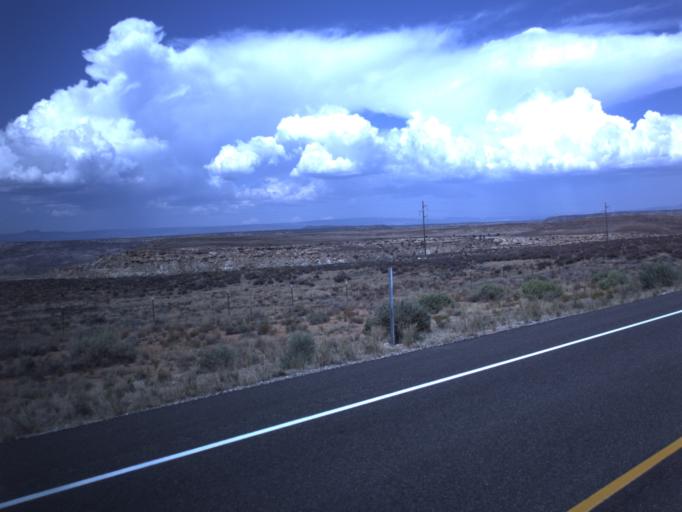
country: US
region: Utah
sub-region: San Juan County
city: Blanding
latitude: 37.3878
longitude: -109.5004
